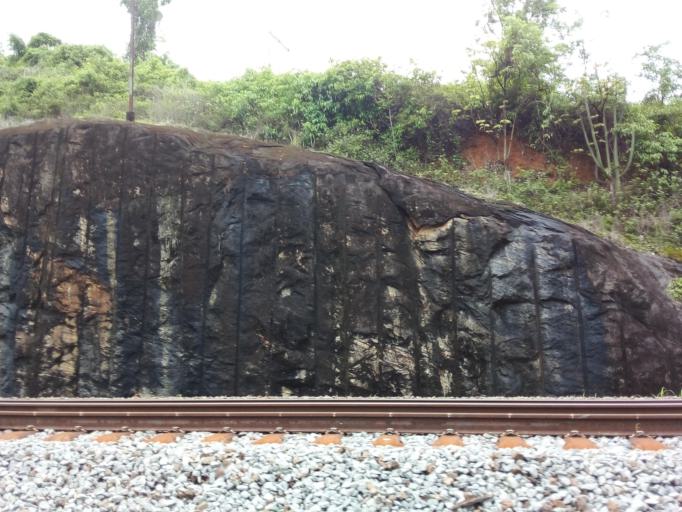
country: BR
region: Espirito Santo
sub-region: Colatina
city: Colatina
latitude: -19.5513
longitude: -40.5843
